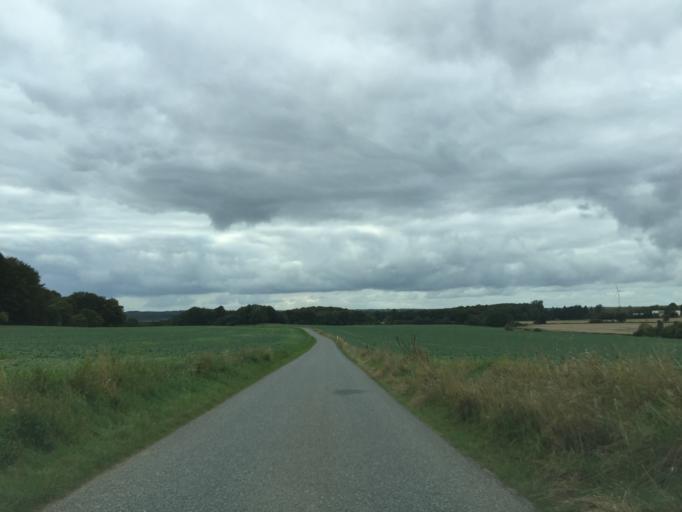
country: DK
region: Central Jutland
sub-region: Silkeborg Kommune
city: Svejbaek
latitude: 56.2408
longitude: 9.6992
